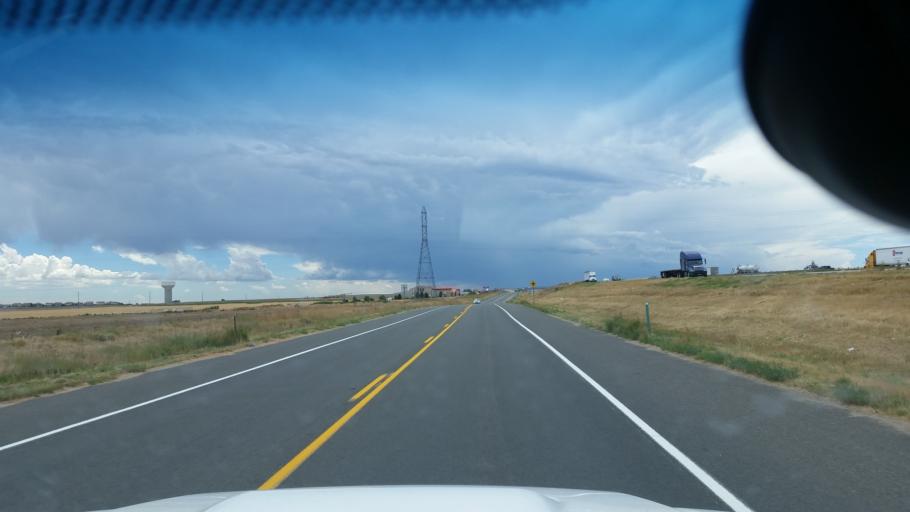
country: US
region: Colorado
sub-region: Weld County
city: Dacono
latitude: 40.0609
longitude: -104.9799
